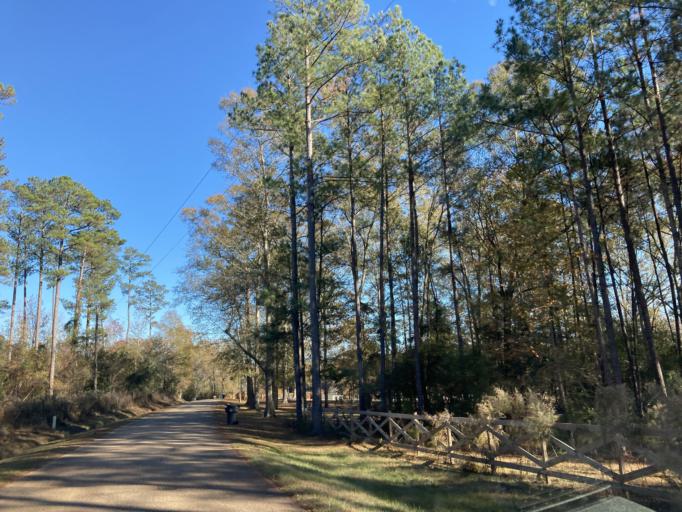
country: US
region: Mississippi
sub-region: Lamar County
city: Sumrall
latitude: 31.3317
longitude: -89.6252
